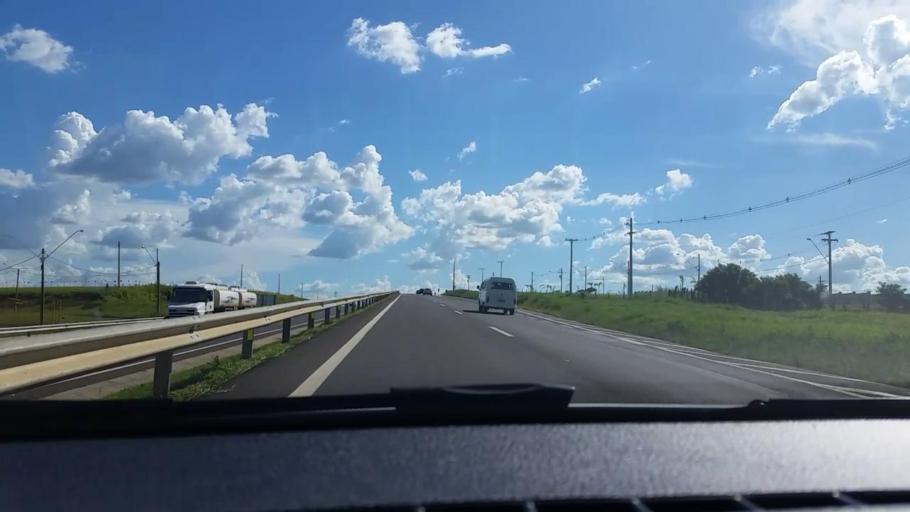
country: BR
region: Sao Paulo
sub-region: Bauru
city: Bauru
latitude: -22.3892
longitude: -49.0762
